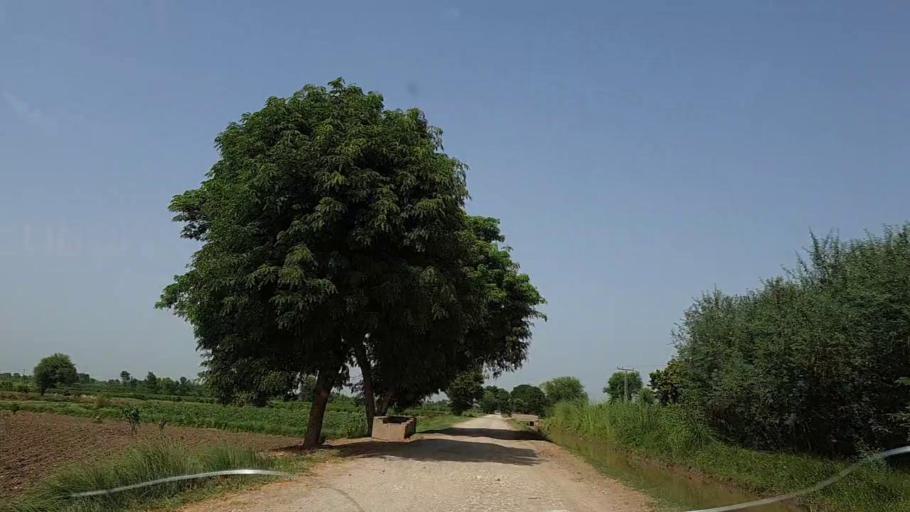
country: PK
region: Sindh
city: Kandiaro
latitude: 27.0417
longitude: 68.1605
